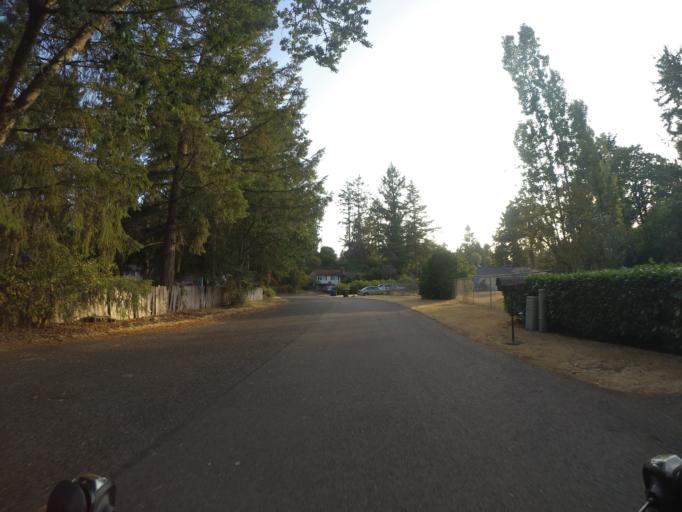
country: US
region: Washington
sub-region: Pierce County
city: Lakewood
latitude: 47.1479
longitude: -122.5181
